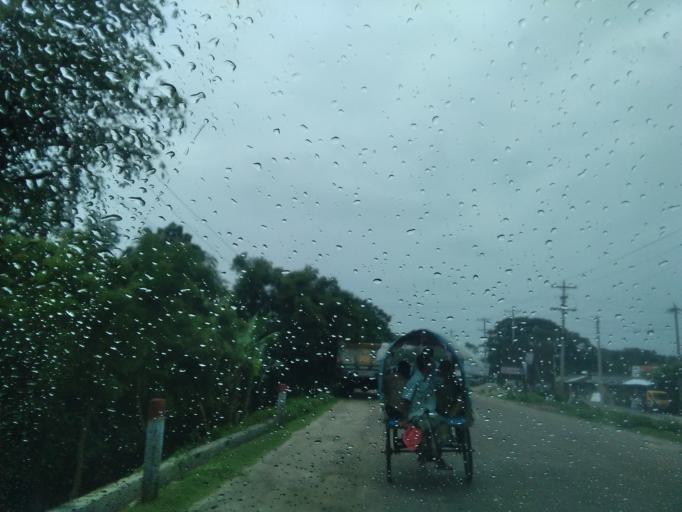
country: IN
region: West Bengal
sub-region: North 24 Parganas
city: Taki
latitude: 22.4562
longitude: 89.0341
